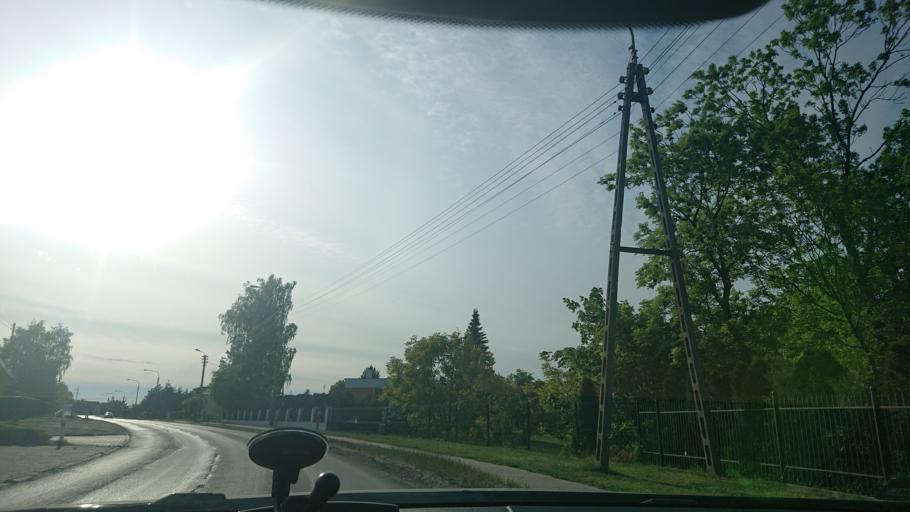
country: PL
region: Greater Poland Voivodeship
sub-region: Powiat gnieznienski
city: Gniezno
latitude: 52.5434
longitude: 17.5738
